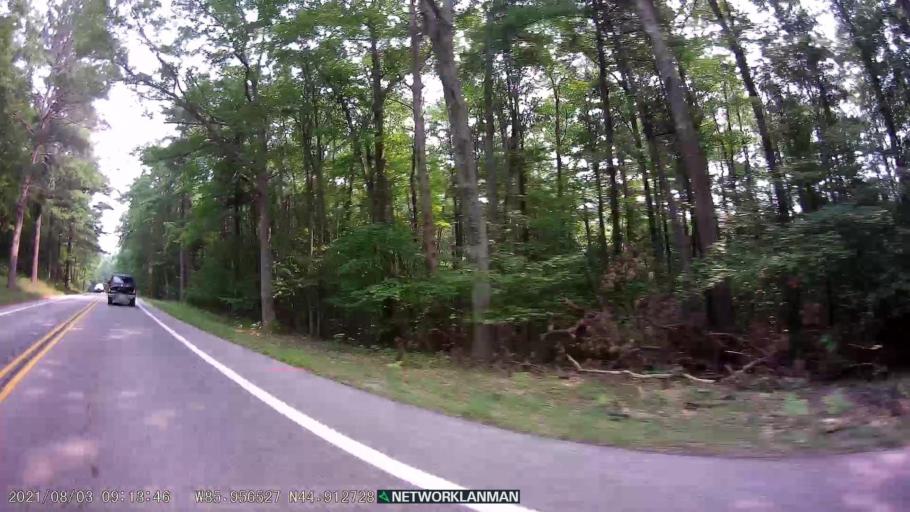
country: US
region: Michigan
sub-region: Leelanau County
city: Leland
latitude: 44.9127
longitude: -85.9566
